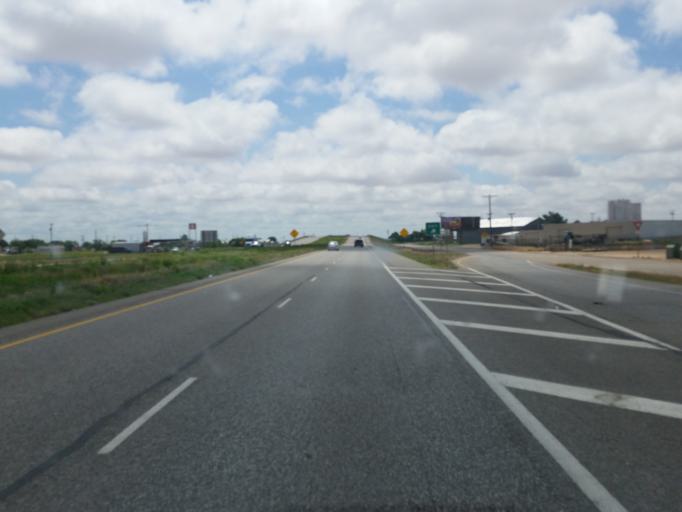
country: US
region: Texas
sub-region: Lubbock County
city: Slaton
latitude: 33.4226
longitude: -101.6476
